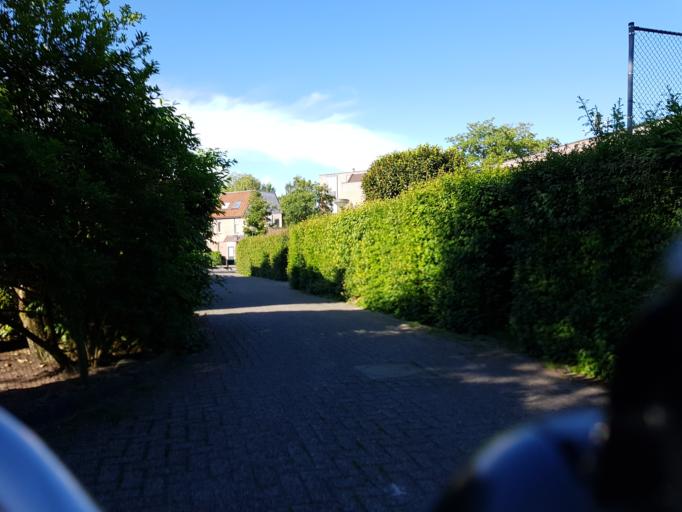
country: NL
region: Gelderland
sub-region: Gemeente Apeldoorn
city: Apeldoorn
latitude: 52.1845
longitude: 5.9980
